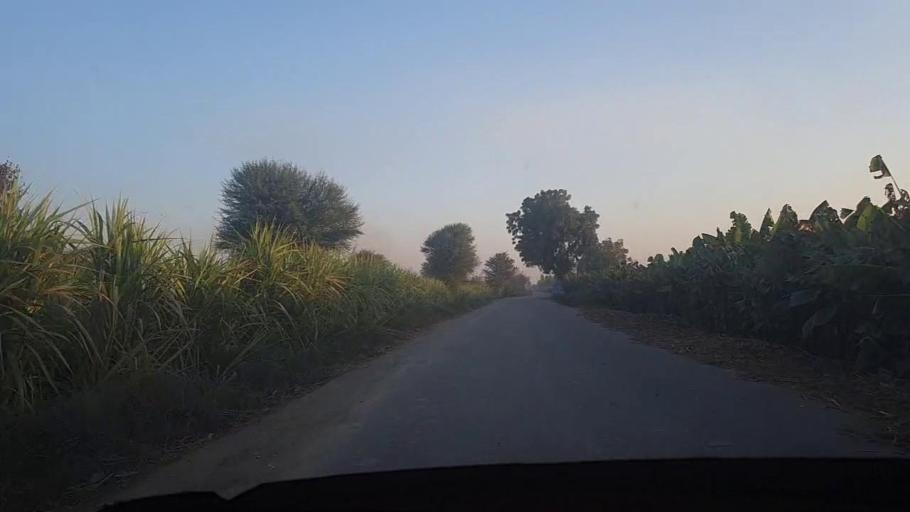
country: PK
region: Sindh
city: Sobhadero
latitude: 27.3472
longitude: 68.3758
